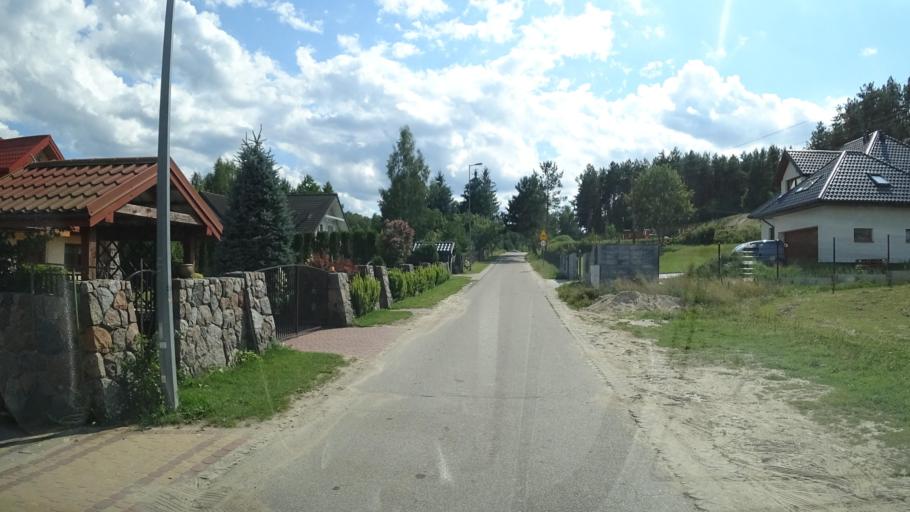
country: PL
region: Podlasie
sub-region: Powiat lomzynski
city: Piatnica
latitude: 53.1432
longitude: 22.1274
